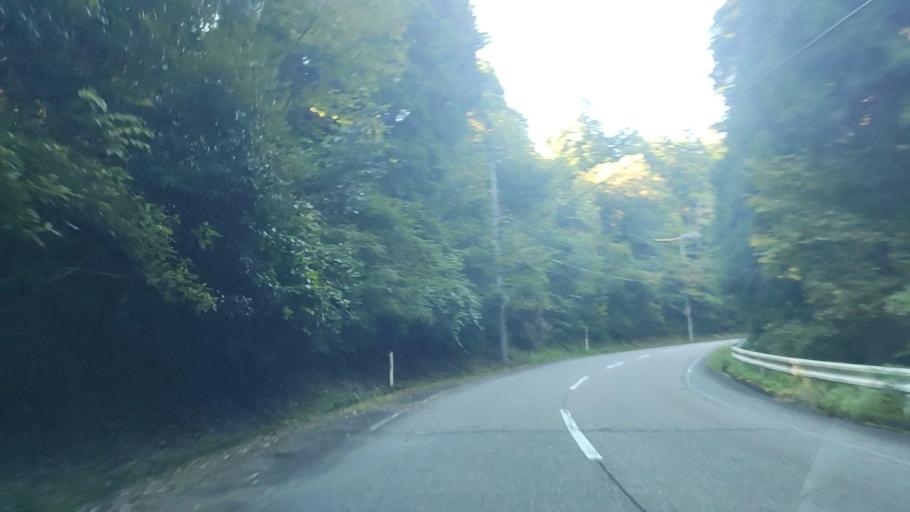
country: JP
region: Ishikawa
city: Nanao
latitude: 37.1107
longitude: 136.9617
